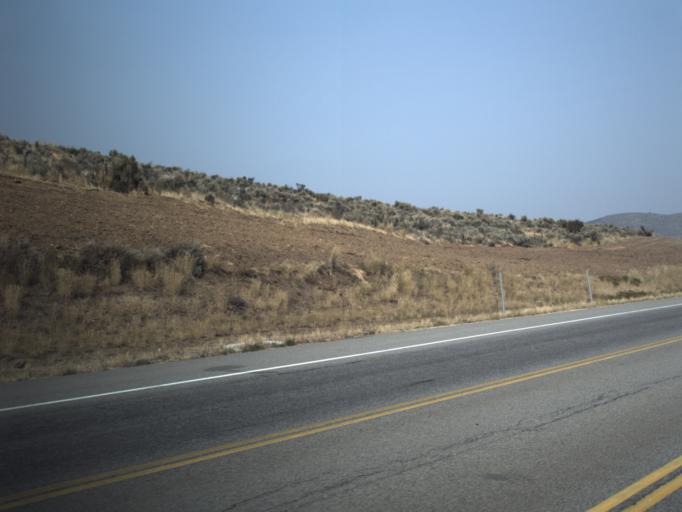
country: US
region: Utah
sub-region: Summit County
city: Park City
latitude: 40.6718
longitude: -111.4729
